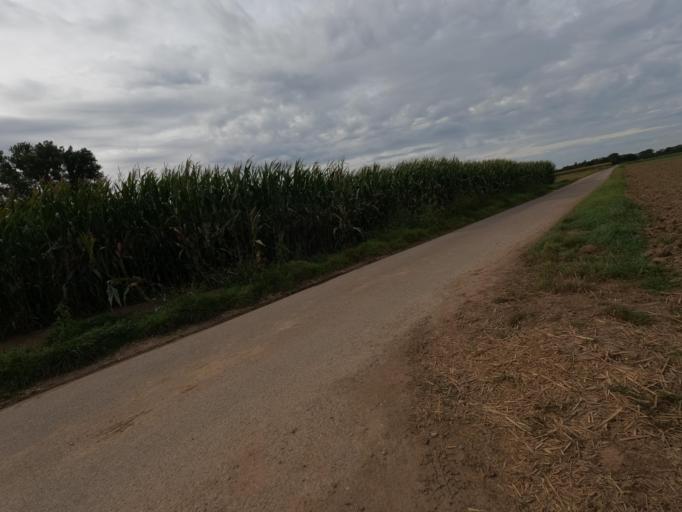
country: DE
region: North Rhine-Westphalia
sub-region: Regierungsbezirk Koln
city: Linnich
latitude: 50.9894
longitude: 6.2661
